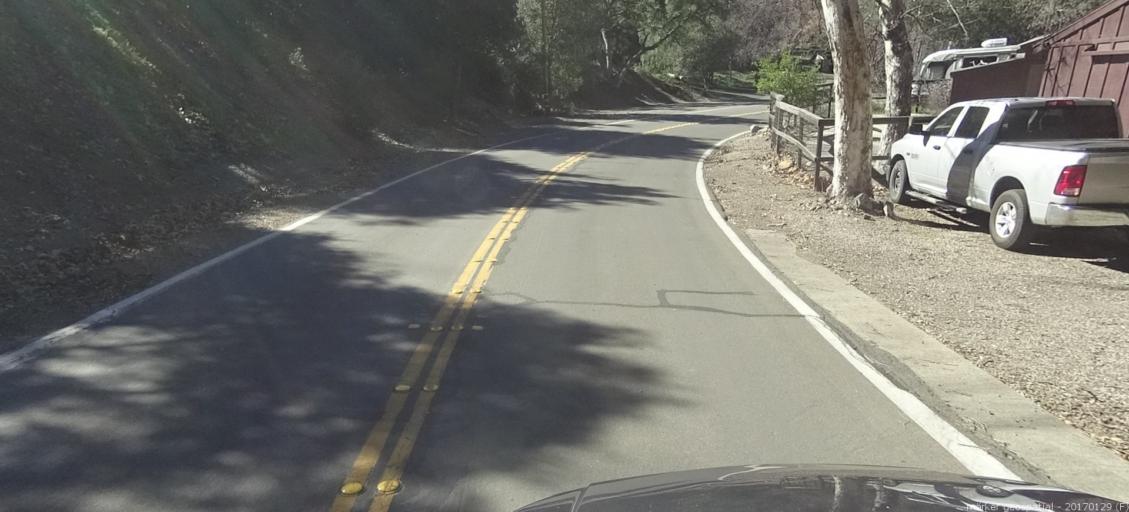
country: US
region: California
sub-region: Orange County
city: Portola Hills
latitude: 33.7461
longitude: -117.5977
